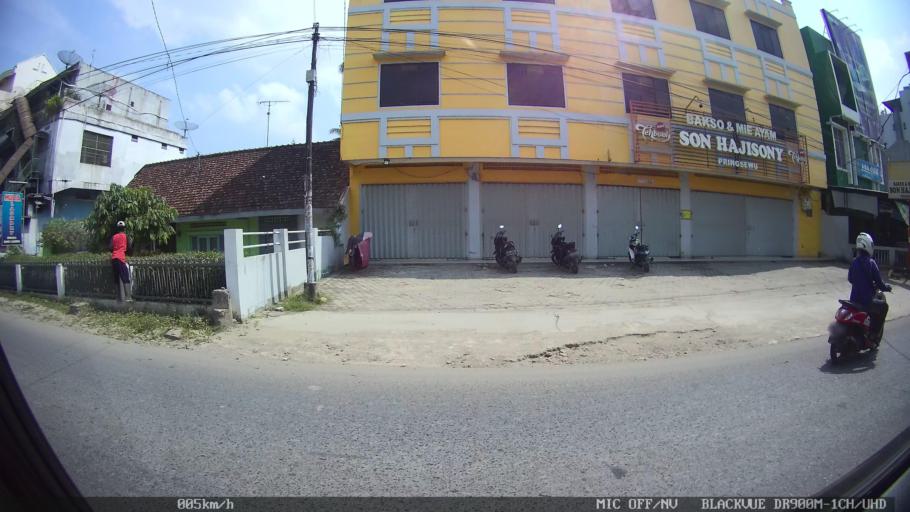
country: ID
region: Lampung
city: Pringsewu
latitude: -5.3568
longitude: 104.9827
